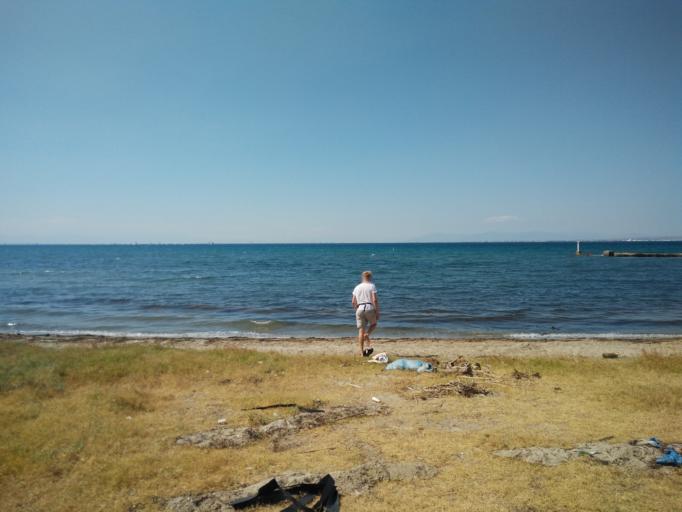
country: GR
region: Central Macedonia
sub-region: Nomos Thessalonikis
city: Kalamaria
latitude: 40.5872
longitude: 22.9398
